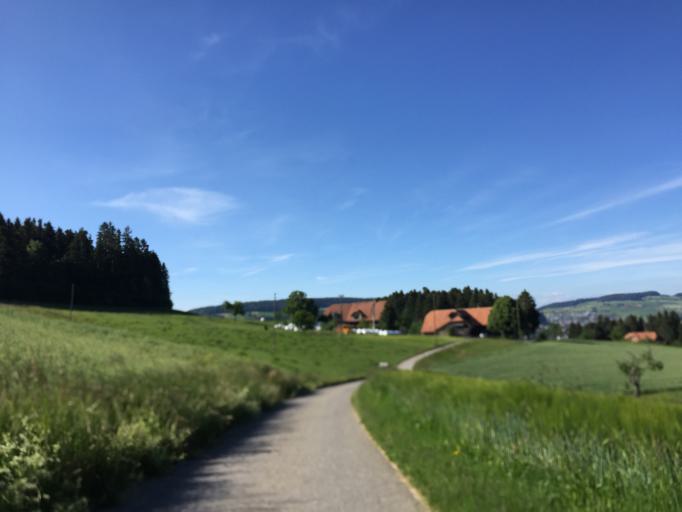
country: CH
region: Bern
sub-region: Bern-Mittelland District
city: Konolfingen
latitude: 46.8611
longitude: 7.6163
